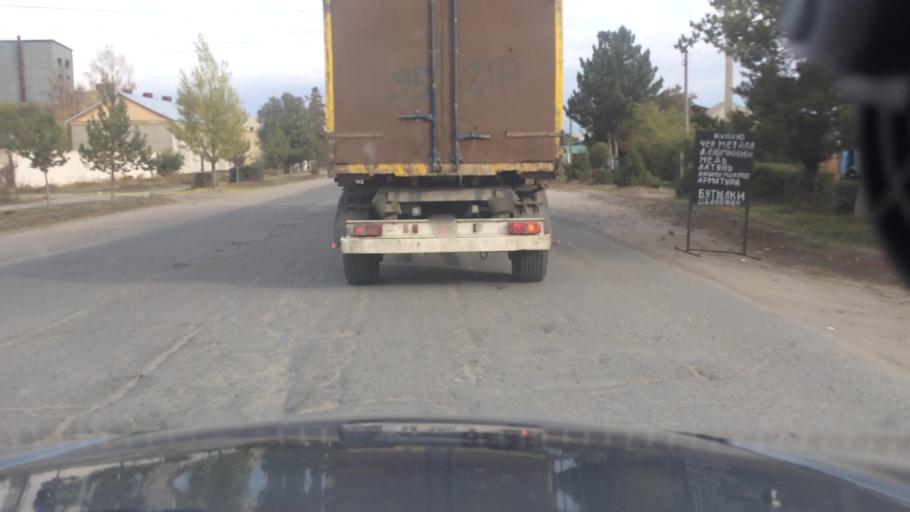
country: KG
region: Ysyk-Koel
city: Karakol
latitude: 42.5139
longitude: 78.3858
